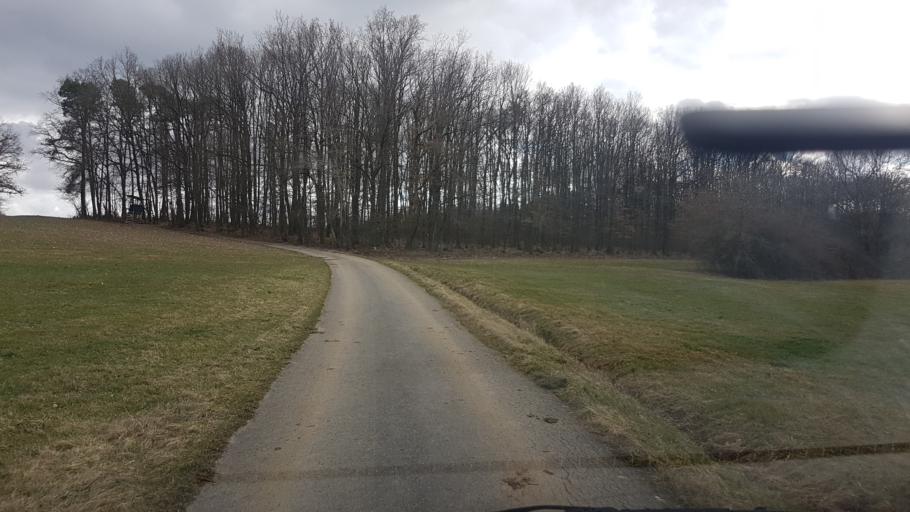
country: DE
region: Bavaria
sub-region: Upper Franconia
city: Hirschaid
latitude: 49.7914
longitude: 10.9719
